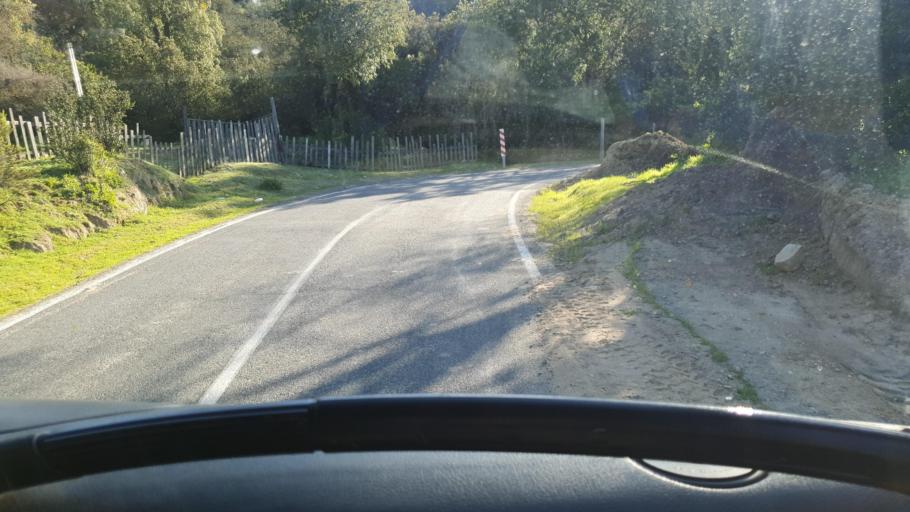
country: CL
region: Valparaiso
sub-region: Provincia de Marga Marga
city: Limache
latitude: -33.2041
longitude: -71.2490
